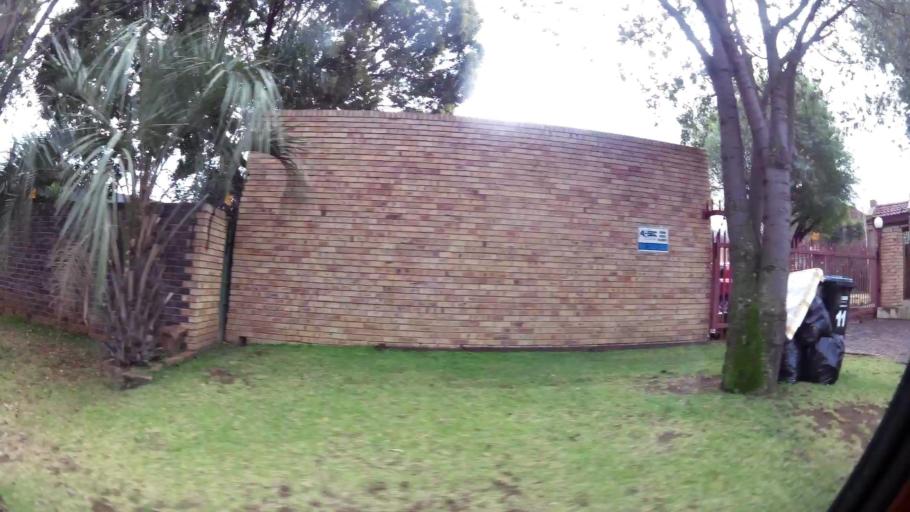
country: ZA
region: Gauteng
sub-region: Sedibeng District Municipality
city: Vanderbijlpark
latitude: -26.7400
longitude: 27.8527
